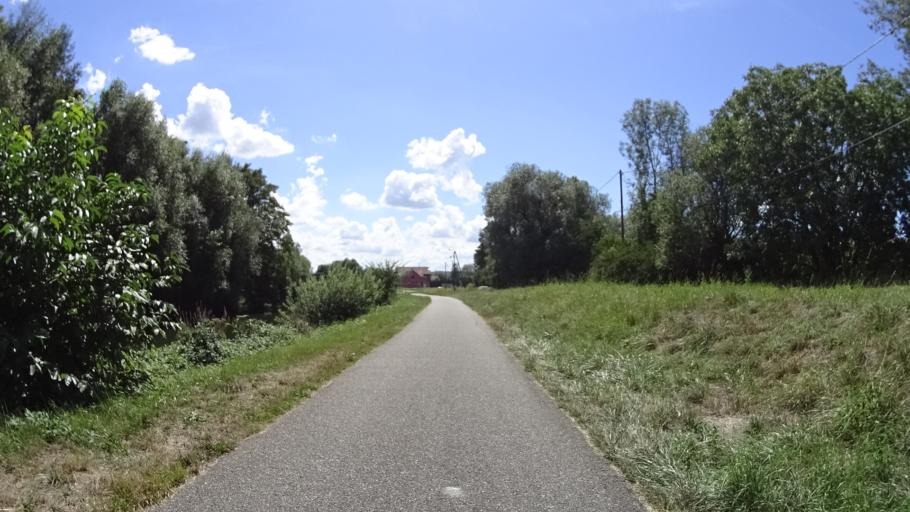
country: FR
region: Alsace
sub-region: Departement du Haut-Rhin
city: Brunstatt
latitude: 47.7214
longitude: 7.3147
